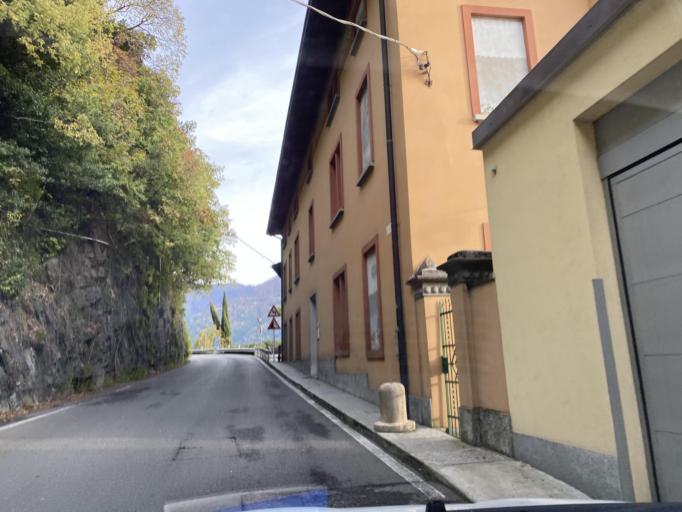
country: IT
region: Lombardy
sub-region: Provincia di Como
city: San Mamete
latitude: 46.0244
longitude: 9.0551
